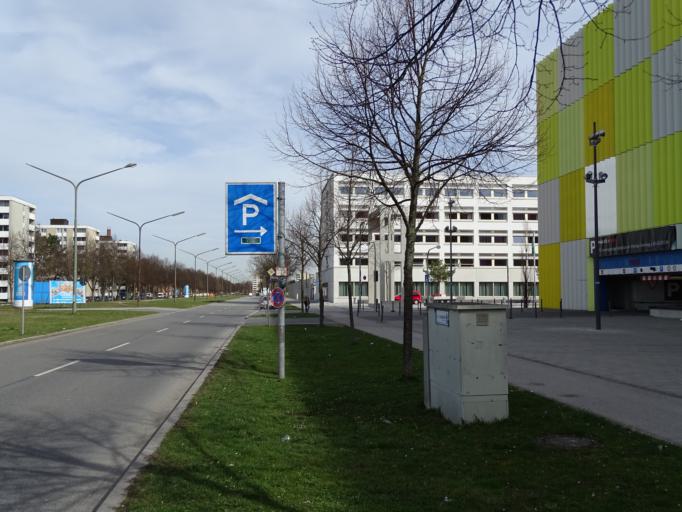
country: DE
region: Bavaria
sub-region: Upper Bavaria
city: Oberschleissheim
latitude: 48.2130
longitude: 11.5626
